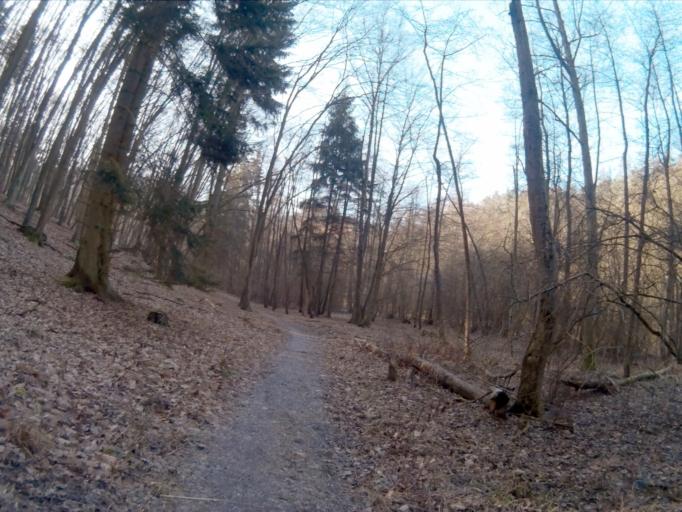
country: CZ
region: Vysocina
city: Namest' nad Oslavou
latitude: 49.1781
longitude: 16.1579
